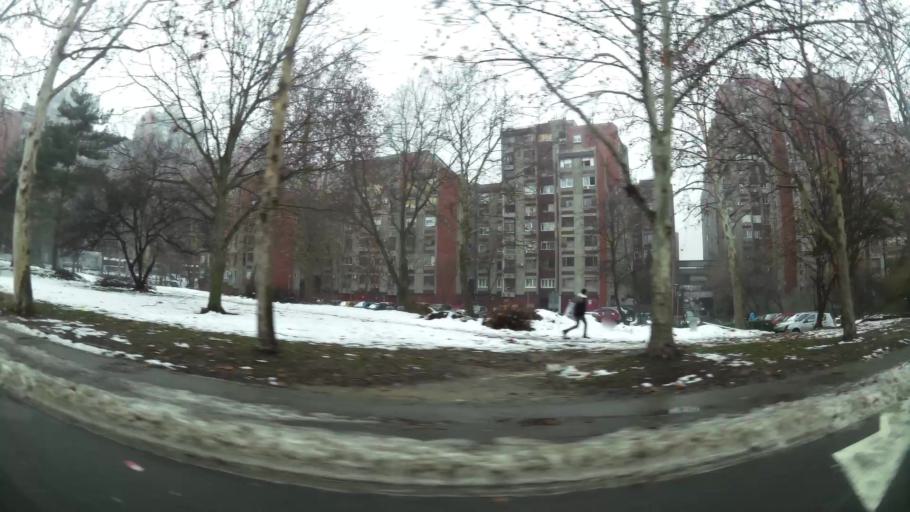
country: RS
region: Central Serbia
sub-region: Belgrade
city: Vozdovac
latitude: 44.7604
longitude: 20.4806
